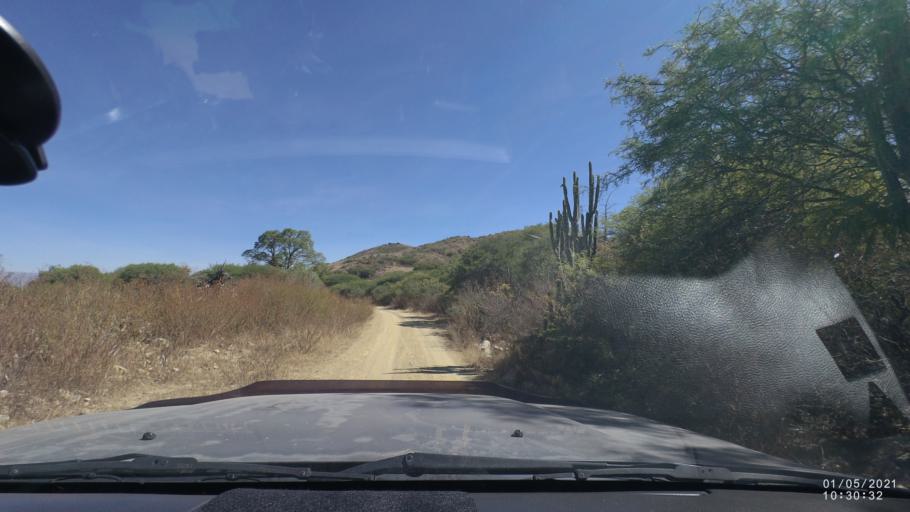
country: BO
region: Cochabamba
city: Capinota
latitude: -17.5930
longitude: -66.1918
